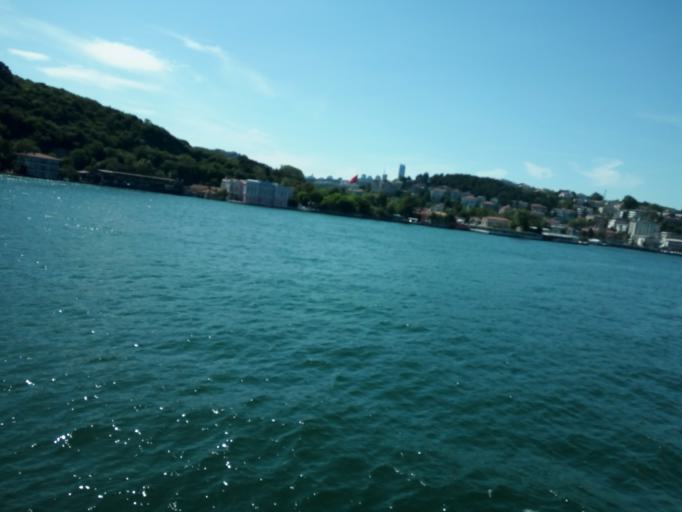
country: TR
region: Istanbul
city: Sisli
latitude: 41.0947
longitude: 29.0580
